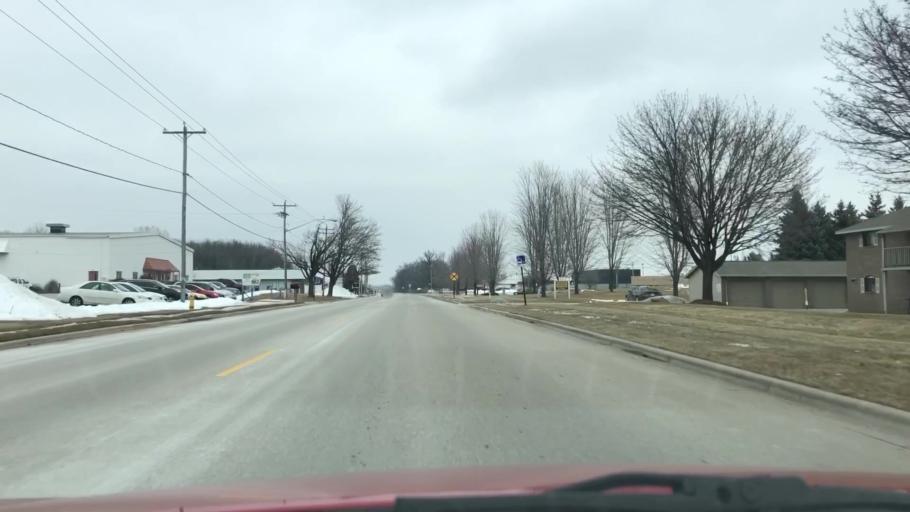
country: US
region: Wisconsin
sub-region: Brown County
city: Ashwaubenon
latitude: 44.4662
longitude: -88.0757
